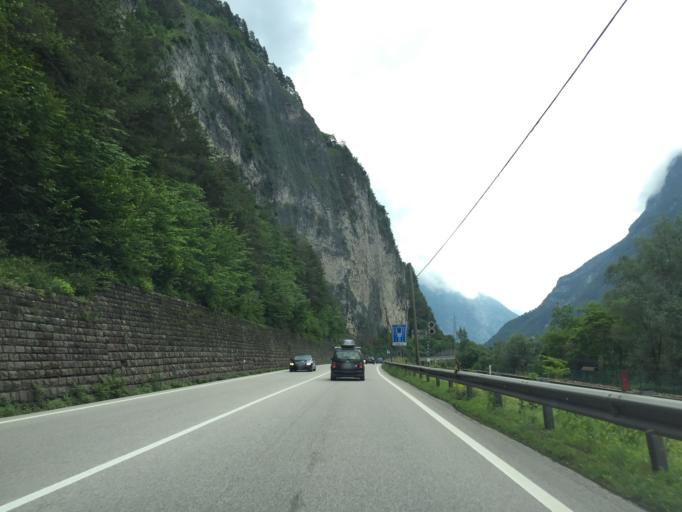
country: IT
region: Trentino-Alto Adige
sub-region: Provincia di Trento
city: Grigno
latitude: 46.0207
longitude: 11.6032
